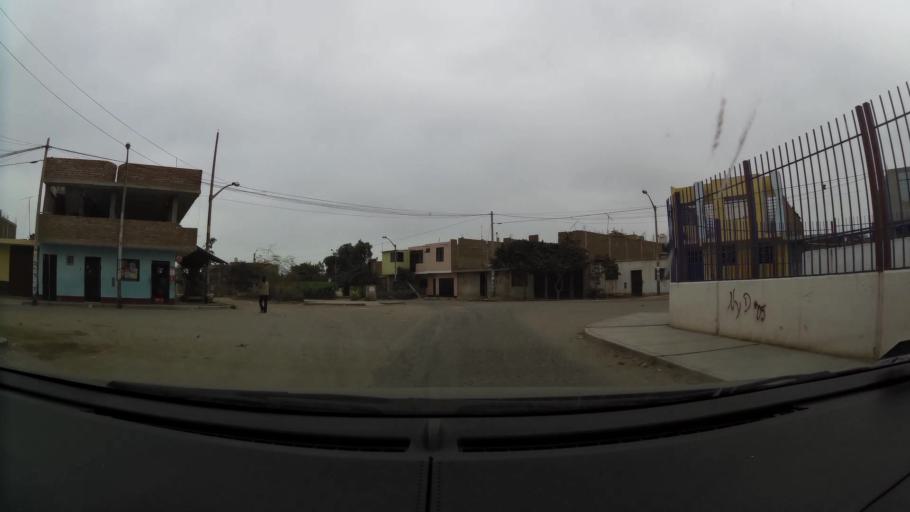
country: PE
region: La Libertad
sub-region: Provincia de Trujillo
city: La Esperanza
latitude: -8.0791
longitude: -79.0586
